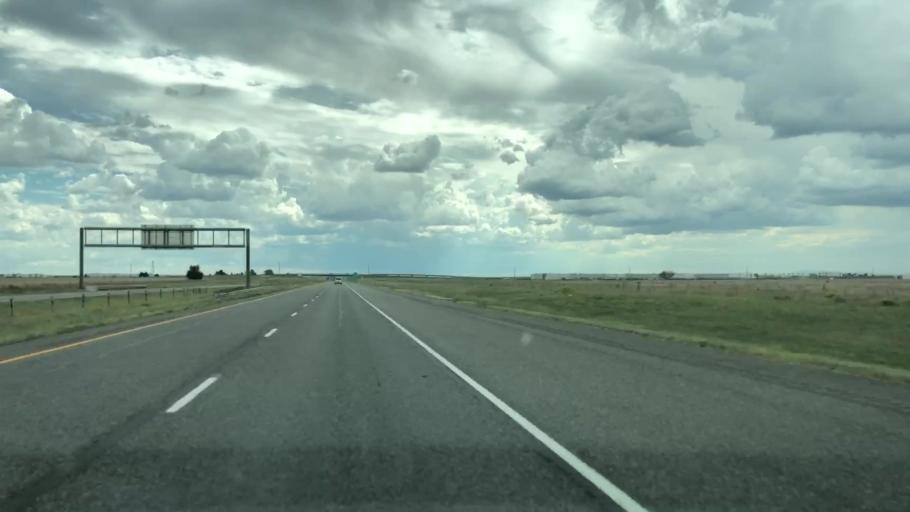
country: US
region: Colorado
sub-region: Adams County
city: Aurora
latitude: 39.7679
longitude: -104.7173
